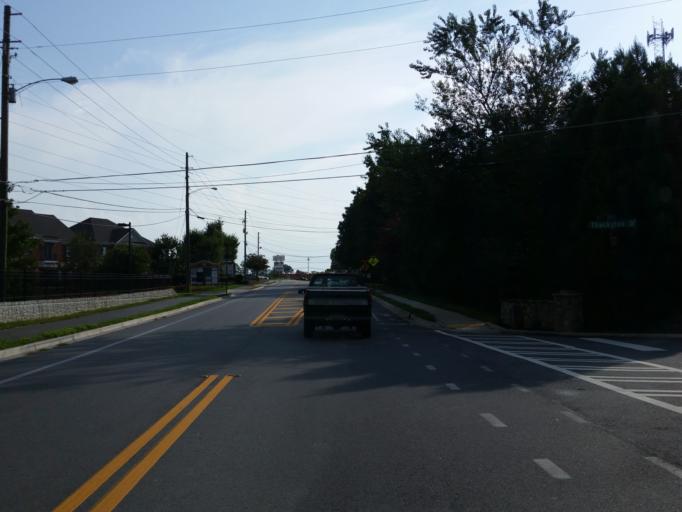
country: US
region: Georgia
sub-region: Fulton County
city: Sandy Springs
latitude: 33.9671
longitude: -84.4041
